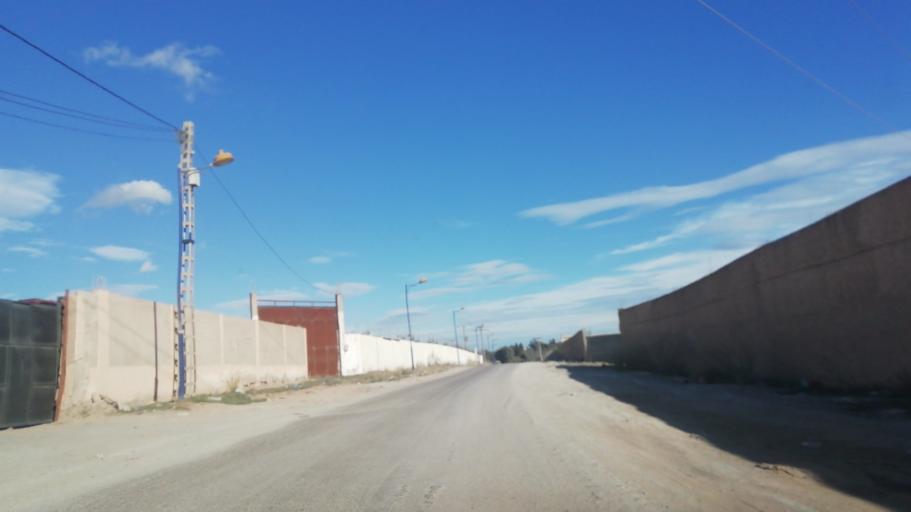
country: DZ
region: Oran
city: Sidi ech Chahmi
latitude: 35.6401
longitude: -0.5446
